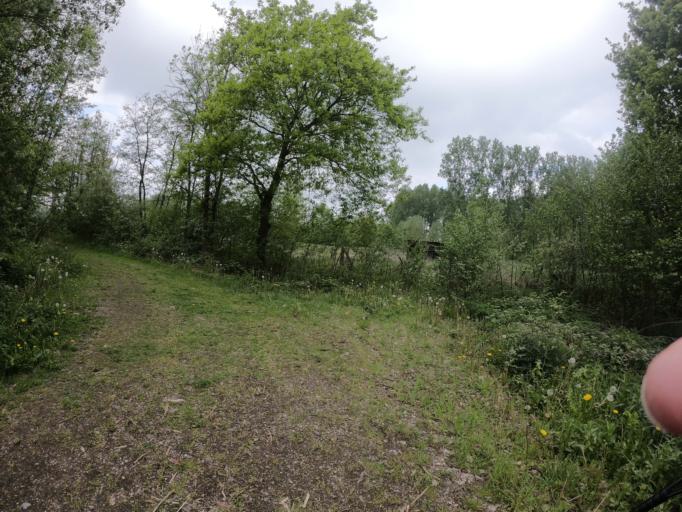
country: BE
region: Flanders
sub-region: Provincie Limburg
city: Diepenbeek
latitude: 50.9018
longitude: 5.4516
